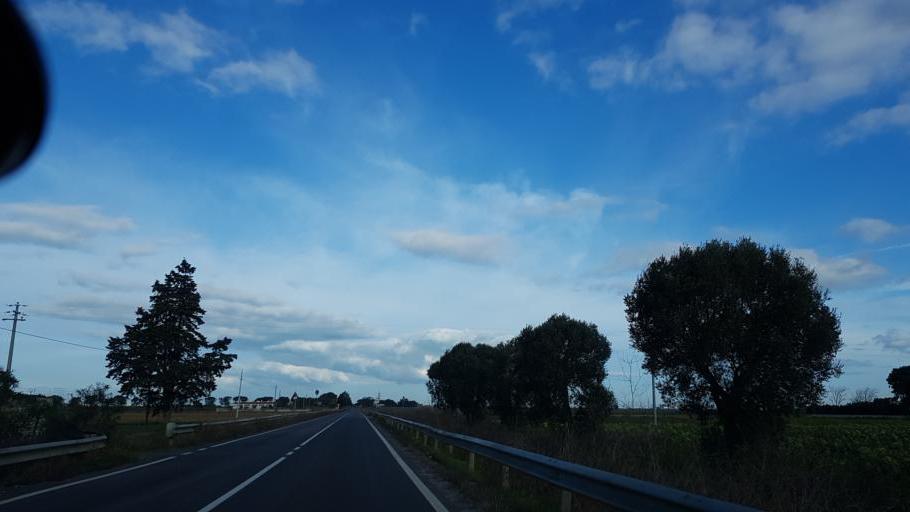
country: IT
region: Apulia
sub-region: Provincia di Brindisi
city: Tuturano
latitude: 40.5732
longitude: 17.9674
